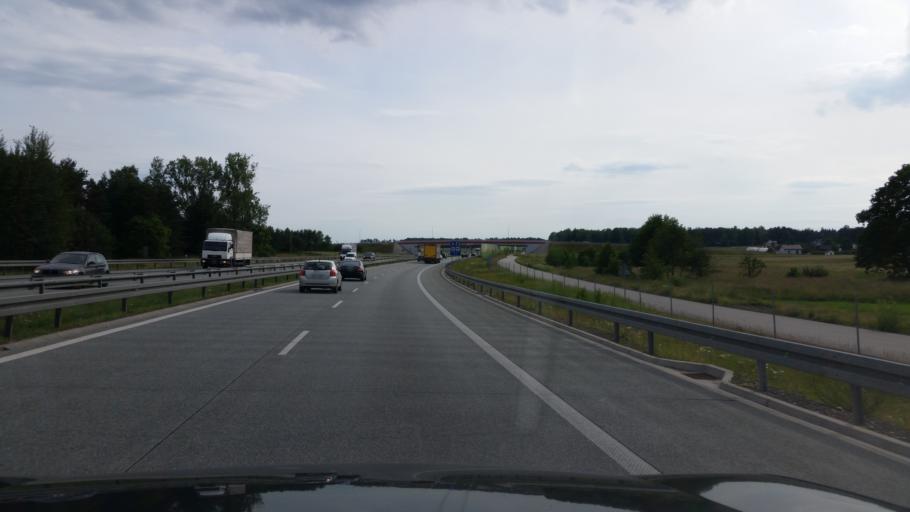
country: PL
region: Lodz Voivodeship
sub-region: Powiat tomaszowski
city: Czerniewice
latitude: 51.6969
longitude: 20.2157
